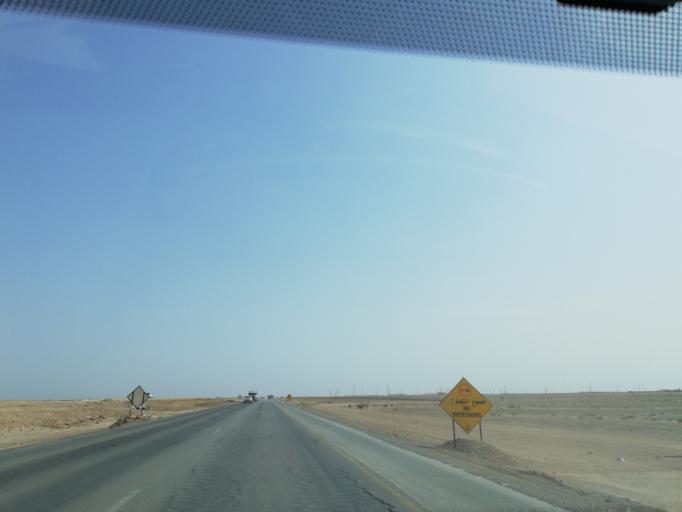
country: OM
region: Muhafazat ad Dakhiliyah
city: Adam
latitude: 21.7411
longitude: 57.3314
